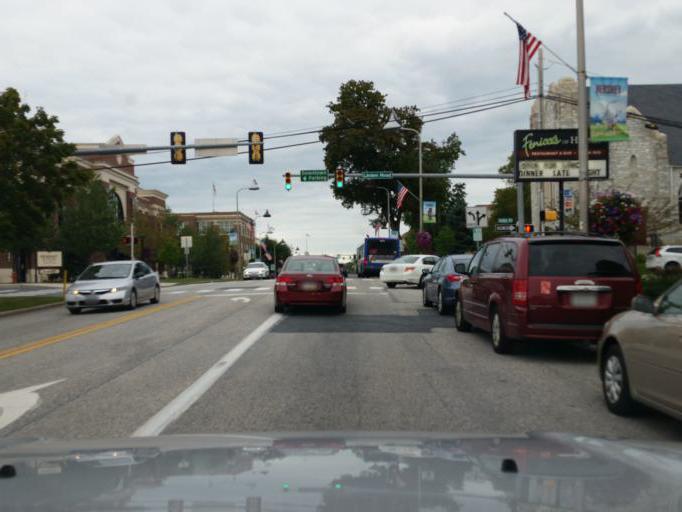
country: US
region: Pennsylvania
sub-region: Dauphin County
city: Hershey
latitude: 40.2846
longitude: -76.6529
